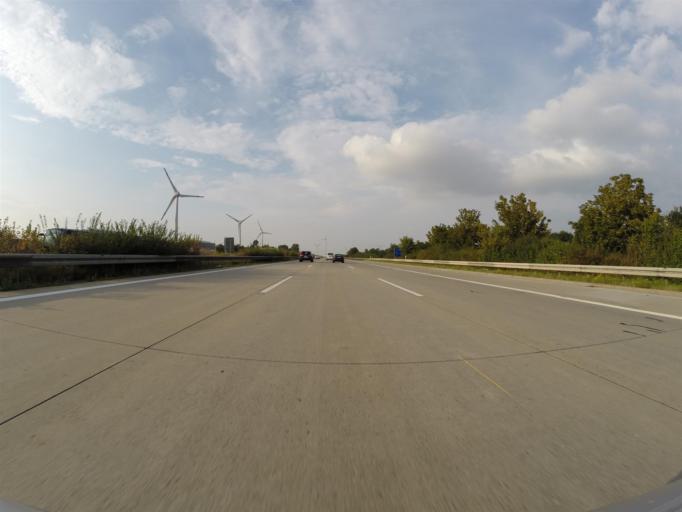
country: DE
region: Saxony-Anhalt
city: Stossen
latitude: 51.1074
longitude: 11.9560
